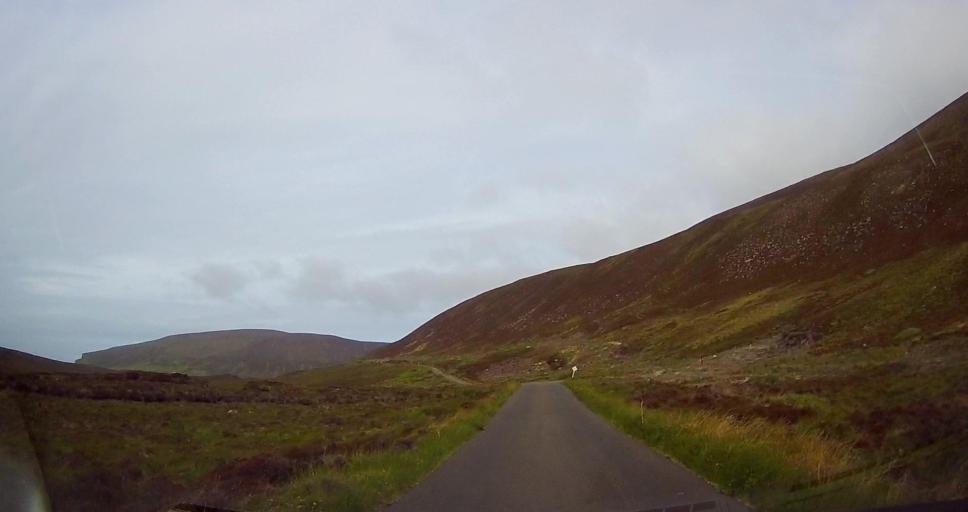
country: GB
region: Scotland
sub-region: Orkney Islands
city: Stromness
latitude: 58.8815
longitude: -3.3490
